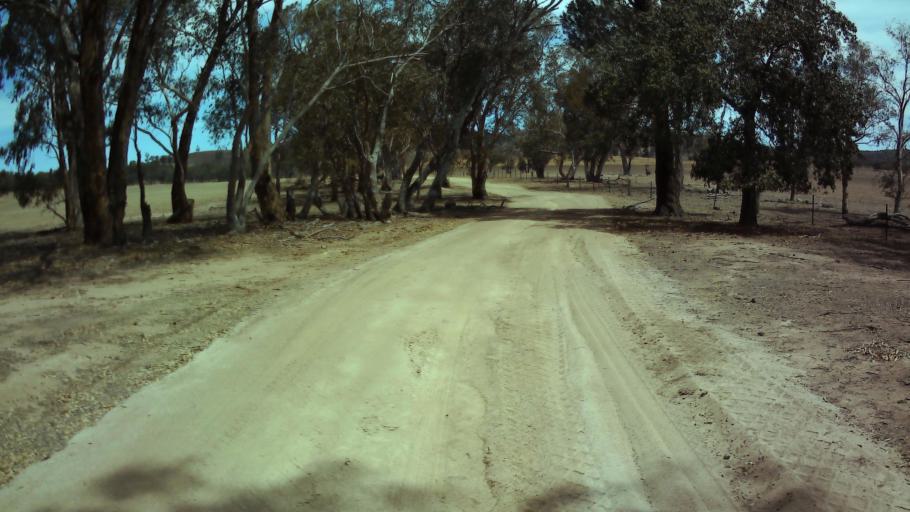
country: AU
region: New South Wales
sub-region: Weddin
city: Grenfell
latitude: -33.7800
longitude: 148.1515
